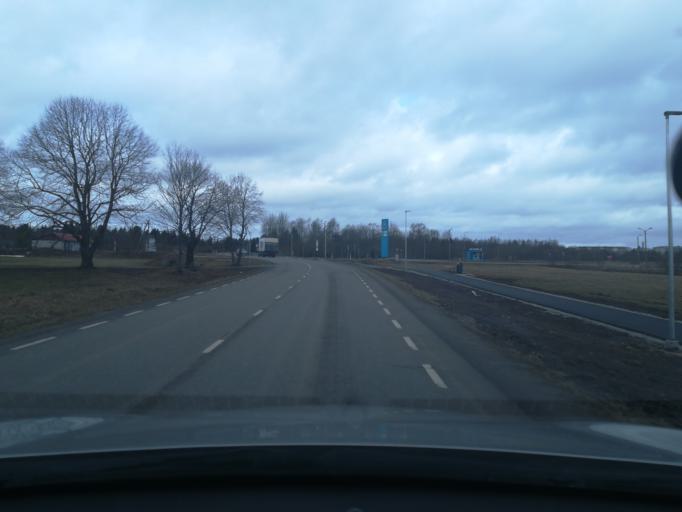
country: EE
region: Harju
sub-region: Harku vald
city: Tabasalu
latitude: 59.4207
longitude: 24.5395
